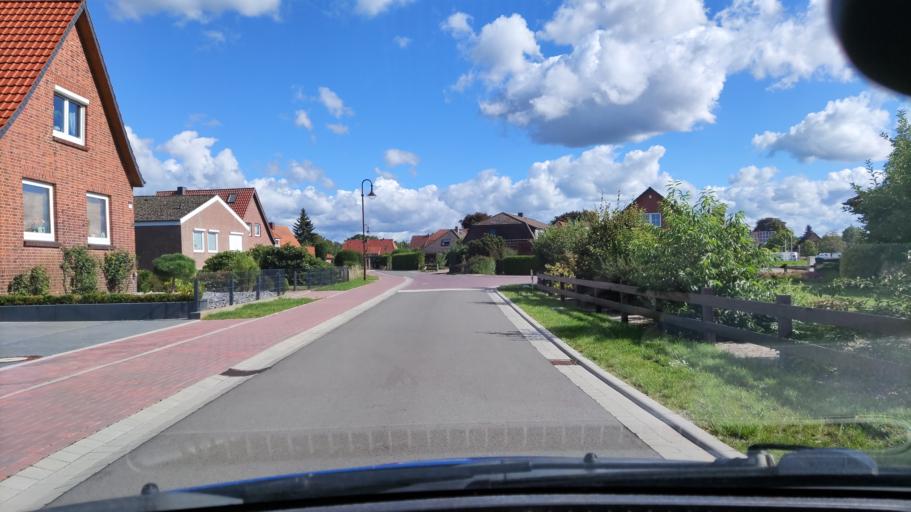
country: DE
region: Lower Saxony
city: Bardowick
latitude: 53.2940
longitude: 10.3834
